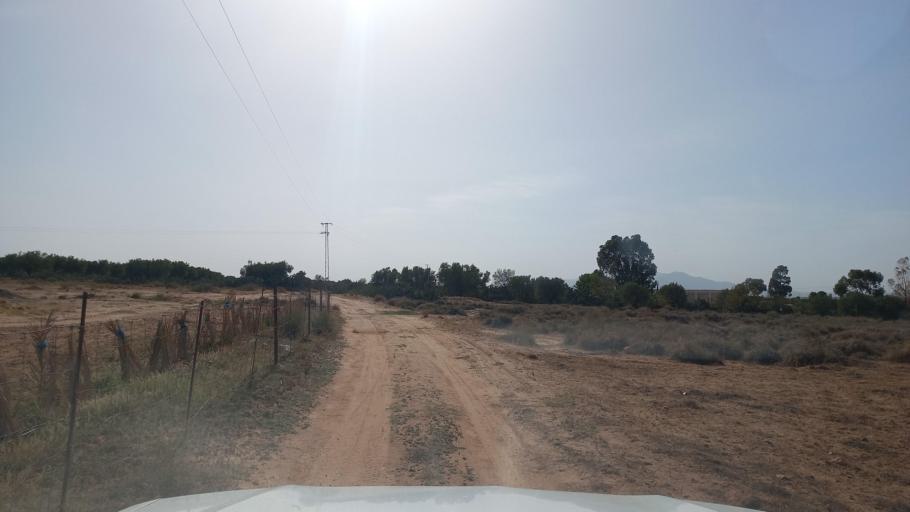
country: TN
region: Al Qasrayn
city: Kasserine
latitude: 35.2057
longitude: 8.9707
